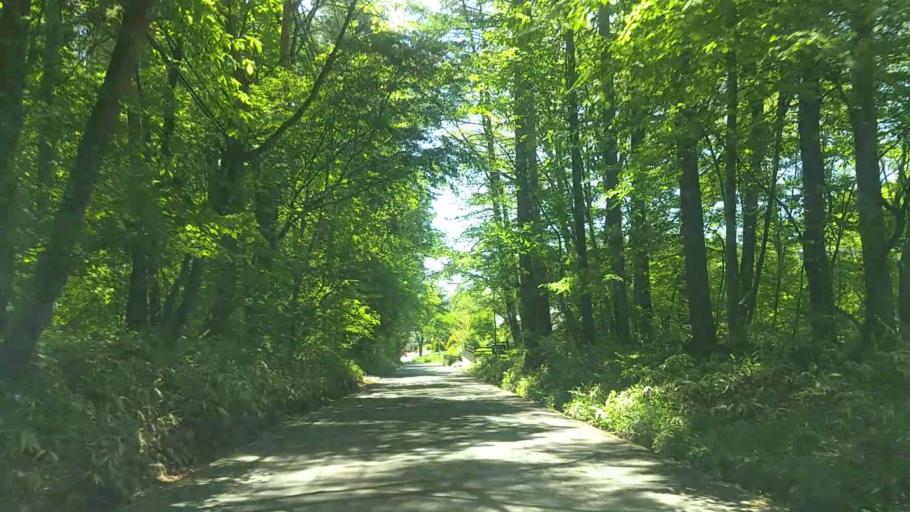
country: JP
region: Yamanashi
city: Nirasaki
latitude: 35.8925
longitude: 138.4378
